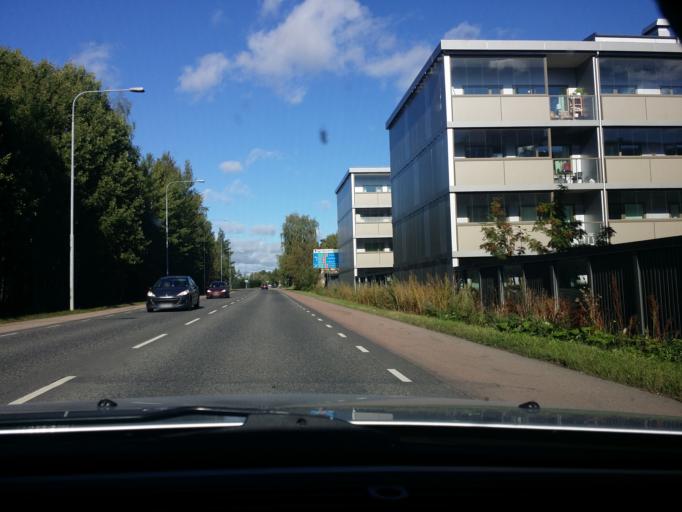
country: SE
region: Vaestmanland
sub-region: Vasteras
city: Vasteras
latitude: 59.6297
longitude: 16.5817
